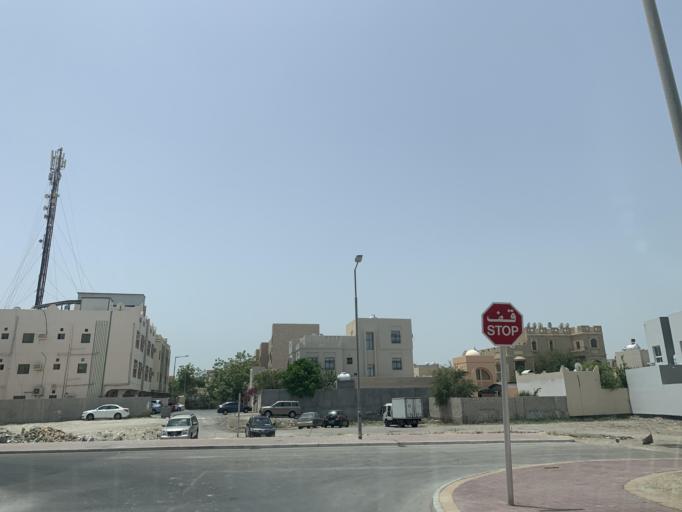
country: BH
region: Northern
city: Sitrah
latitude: 26.1492
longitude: 50.5879
